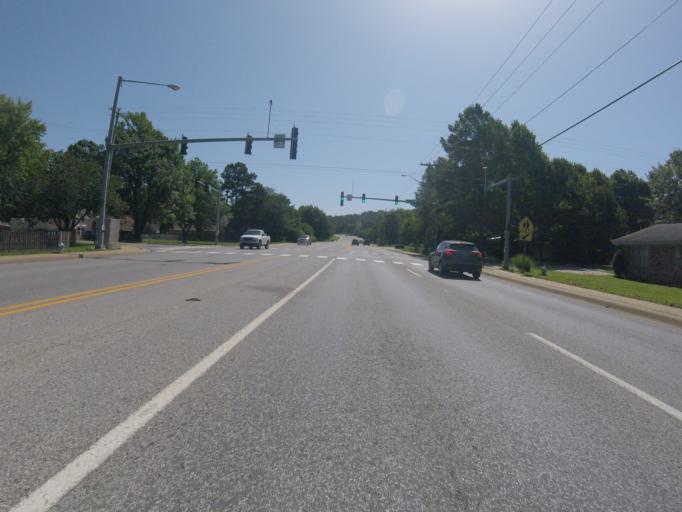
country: US
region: Arkansas
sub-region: Washington County
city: Fayetteville
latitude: 36.0779
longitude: -94.1892
